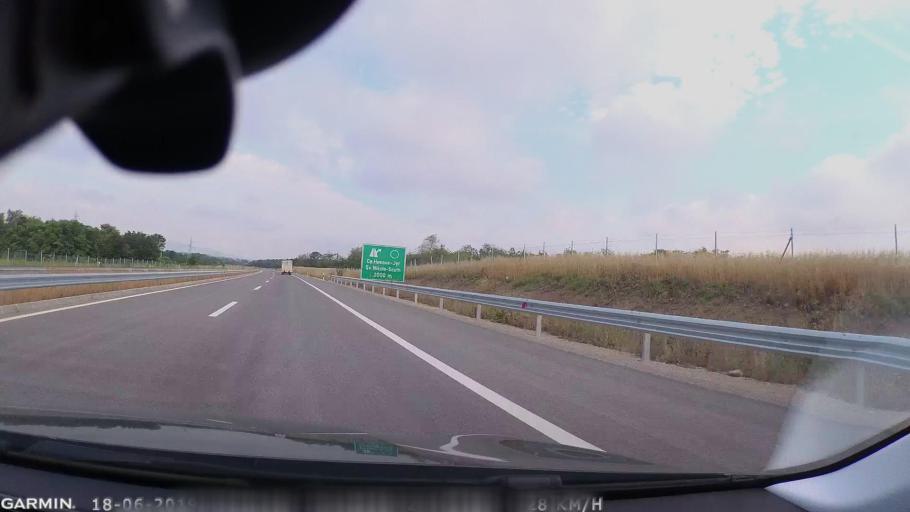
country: MK
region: Sveti Nikole
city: Sveti Nikole
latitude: 41.8428
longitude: 21.9790
